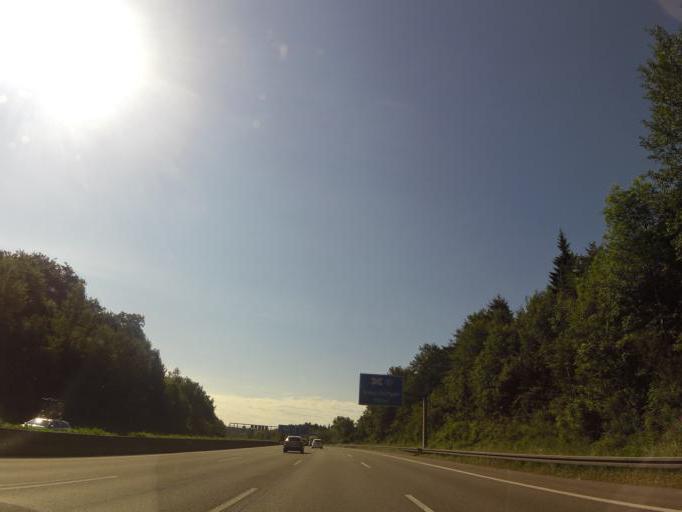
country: DE
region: Baden-Wuerttemberg
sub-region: Regierungsbezirk Stuttgart
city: Sindelfingen
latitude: 48.7376
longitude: 9.0385
